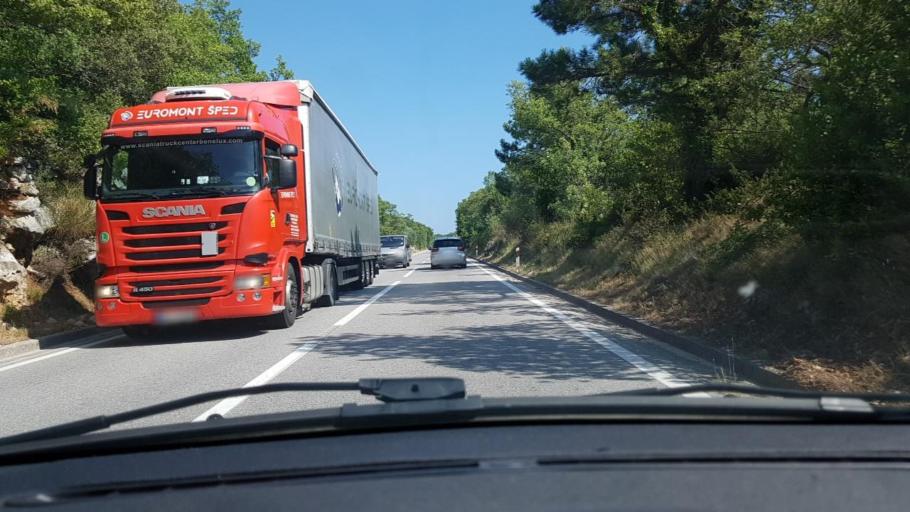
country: HR
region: Dubrovacko-Neretvanska
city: Podgora
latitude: 42.8211
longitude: 17.7690
